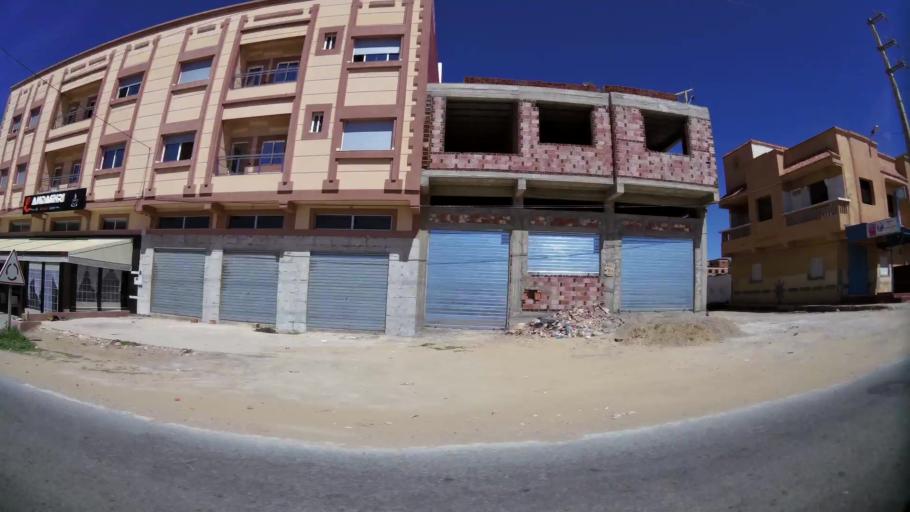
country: MA
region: Oriental
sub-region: Berkane-Taourirt
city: Madagh
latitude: 35.1308
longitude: -2.4246
